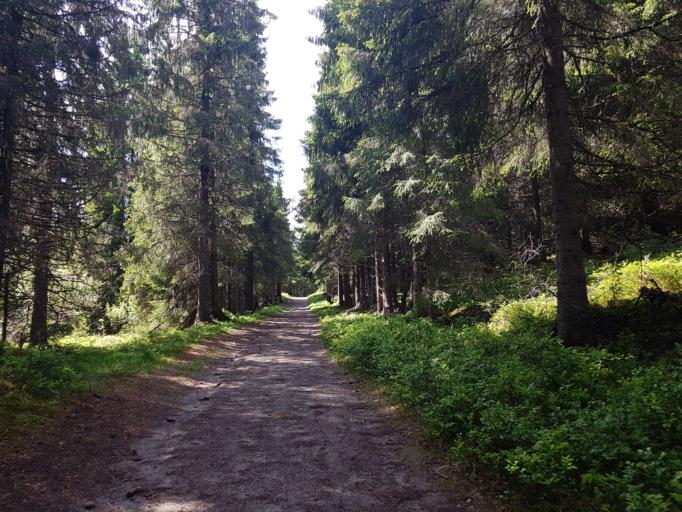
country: NO
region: Sor-Trondelag
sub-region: Trondheim
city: Trondheim
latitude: 63.4183
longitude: 10.3100
